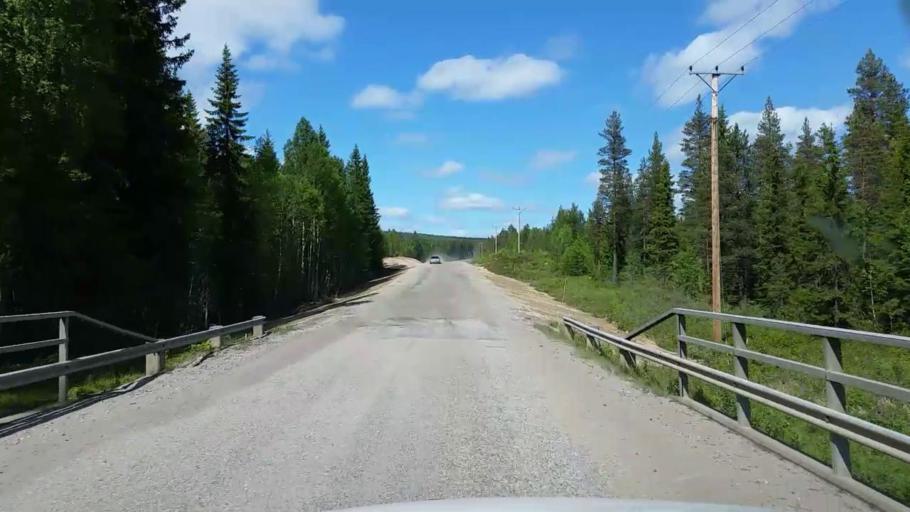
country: SE
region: Gaevleborg
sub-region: Ljusdals Kommun
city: Farila
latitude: 61.5923
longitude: 15.9209
